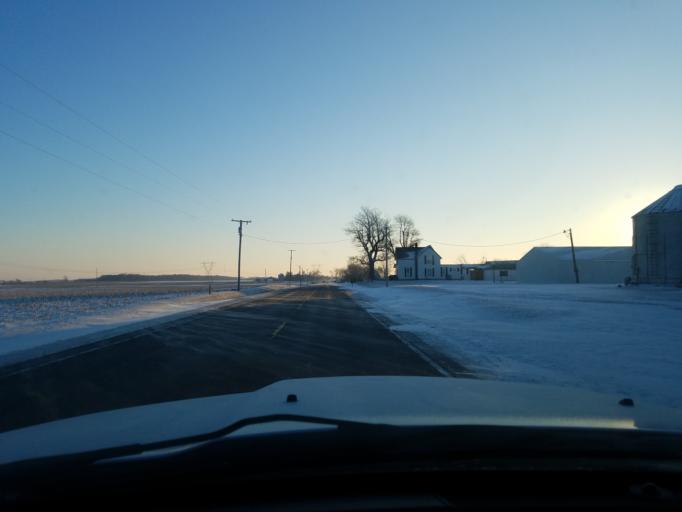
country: US
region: Indiana
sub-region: Marshall County
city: Bremen
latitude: 41.4498
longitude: -86.2456
